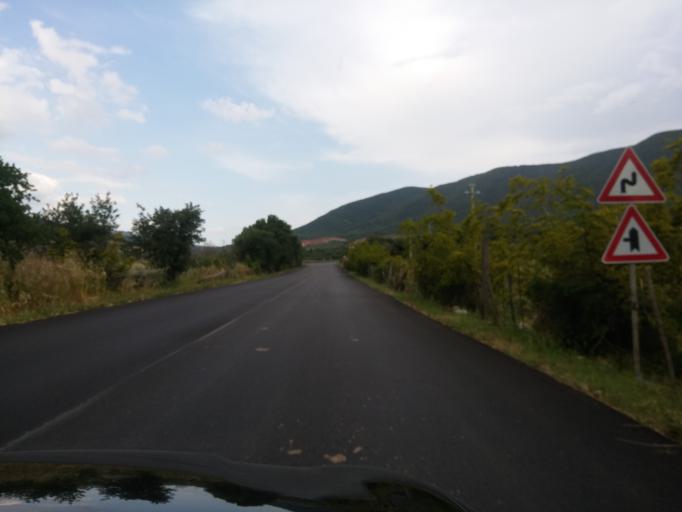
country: IT
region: Apulia
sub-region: Provincia di Foggia
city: Rignano Garganico
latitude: 41.7150
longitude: 15.5416
